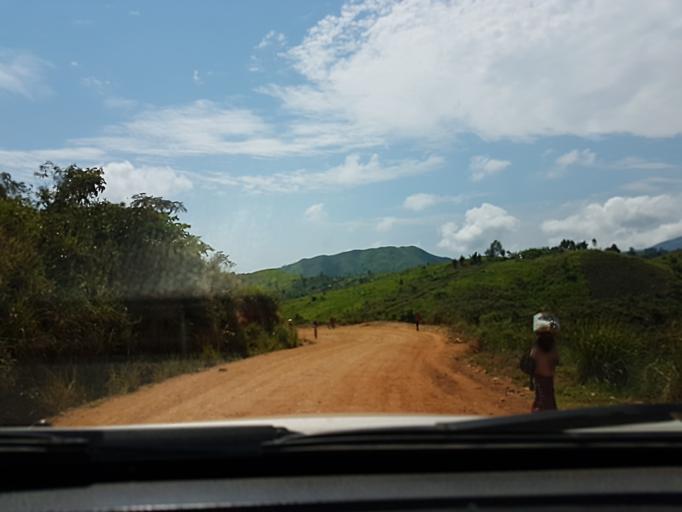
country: RW
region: Western Province
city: Cyangugu
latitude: -2.7038
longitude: 28.9225
